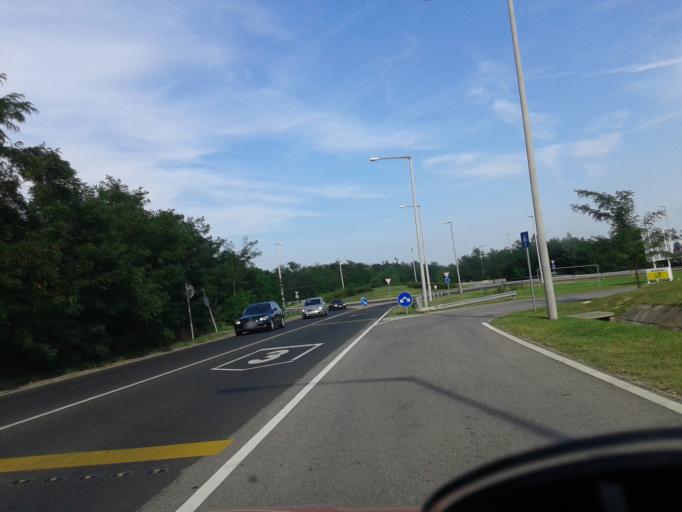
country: HU
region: Pest
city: Godollo
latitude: 47.5921
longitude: 19.3276
